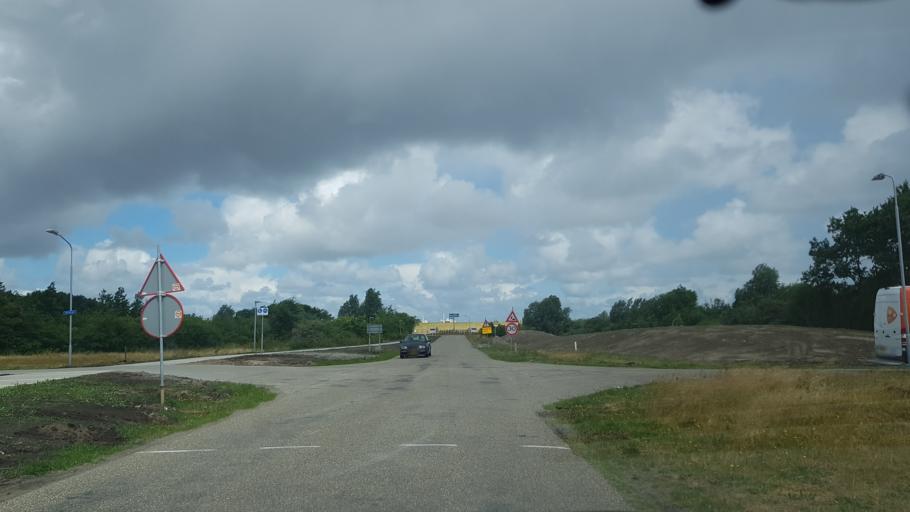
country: NL
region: Friesland
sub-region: Gemeente Dongeradeel
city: Anjum
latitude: 53.4050
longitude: 6.2123
